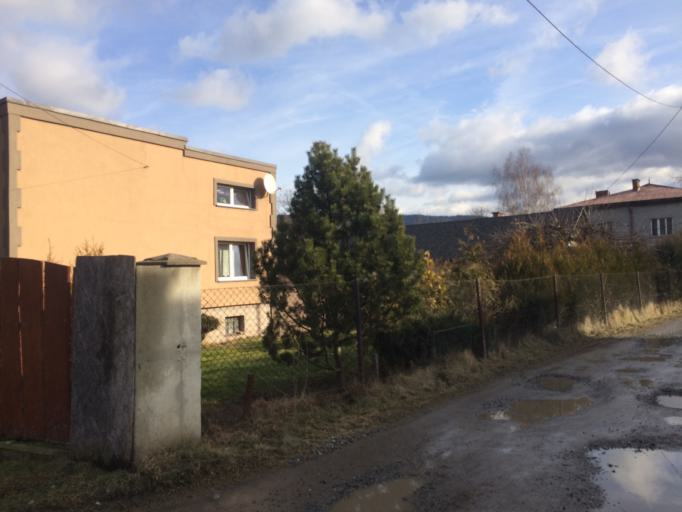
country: PL
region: Silesian Voivodeship
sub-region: Powiat bielski
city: Bystra
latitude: 49.7594
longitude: 19.0690
